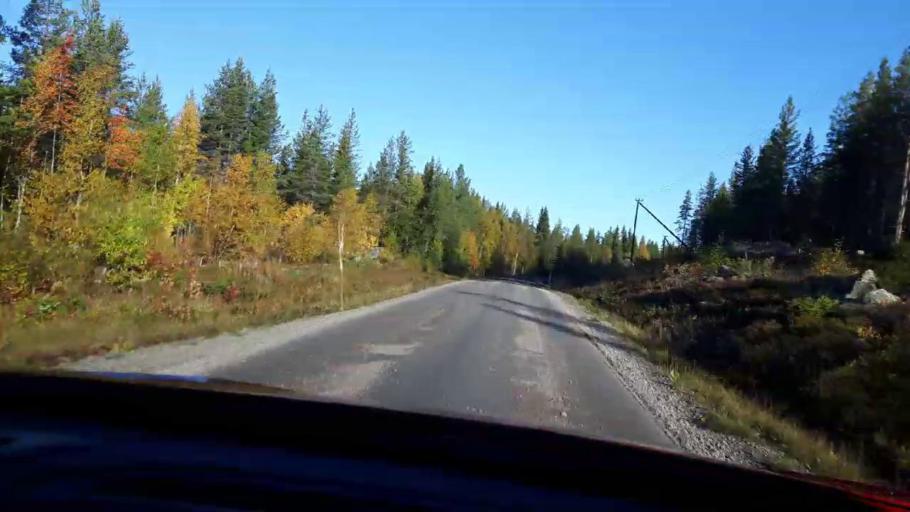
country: SE
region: Jaemtland
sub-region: Stroemsunds Kommun
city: Stroemsund
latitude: 64.3732
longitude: 15.1536
